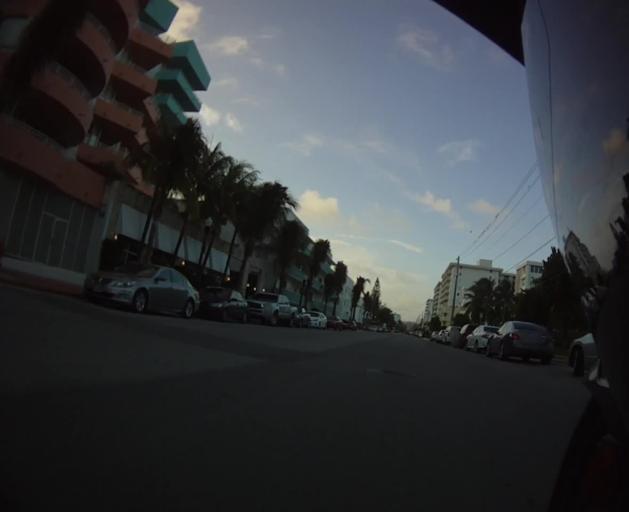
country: US
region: Florida
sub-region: Miami-Dade County
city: Miami Beach
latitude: 25.7713
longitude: -80.1326
